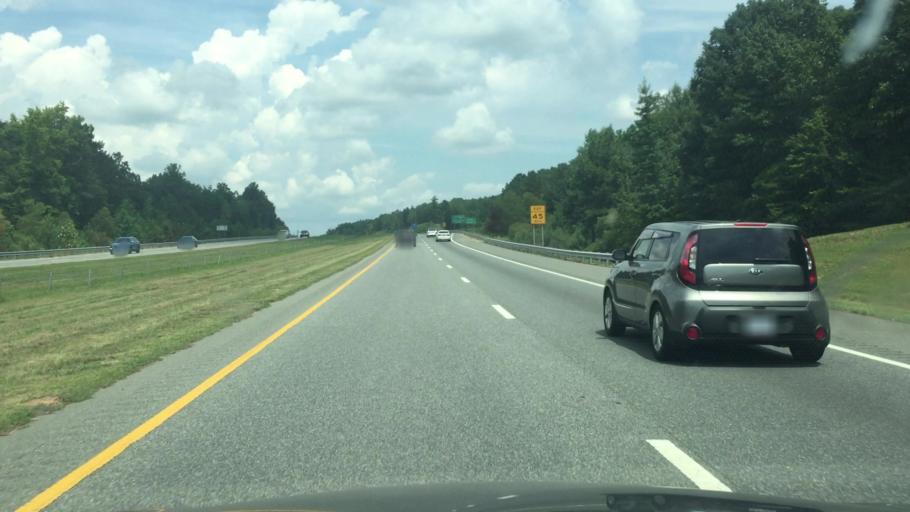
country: US
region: North Carolina
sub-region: Montgomery County
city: Biscoe
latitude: 35.5097
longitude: -79.7811
